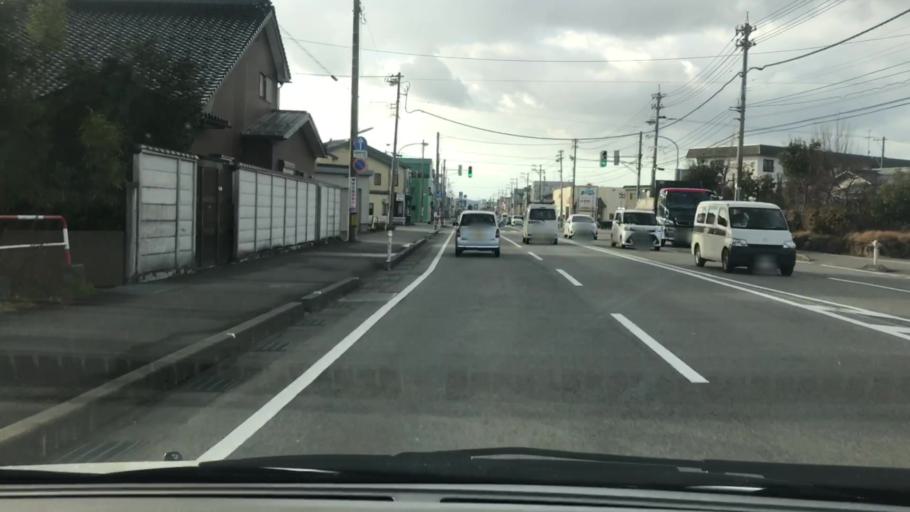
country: JP
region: Toyama
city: Toyama-shi
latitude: 36.6867
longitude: 137.2415
